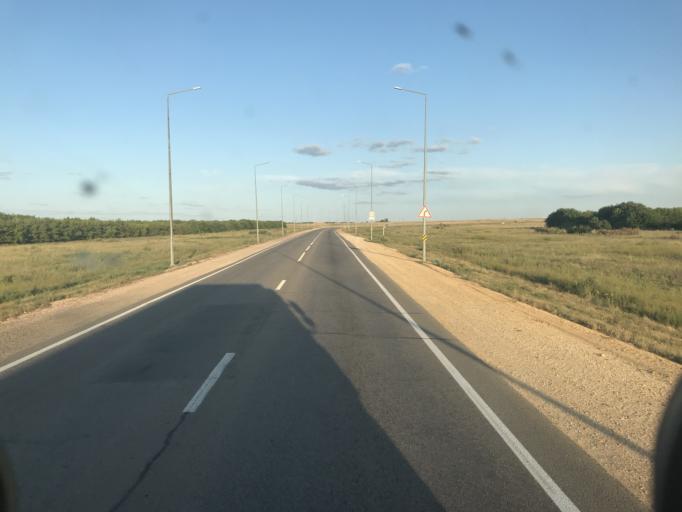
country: KZ
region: Astana Qalasy
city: Astana
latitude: 51.1845
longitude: 71.6052
